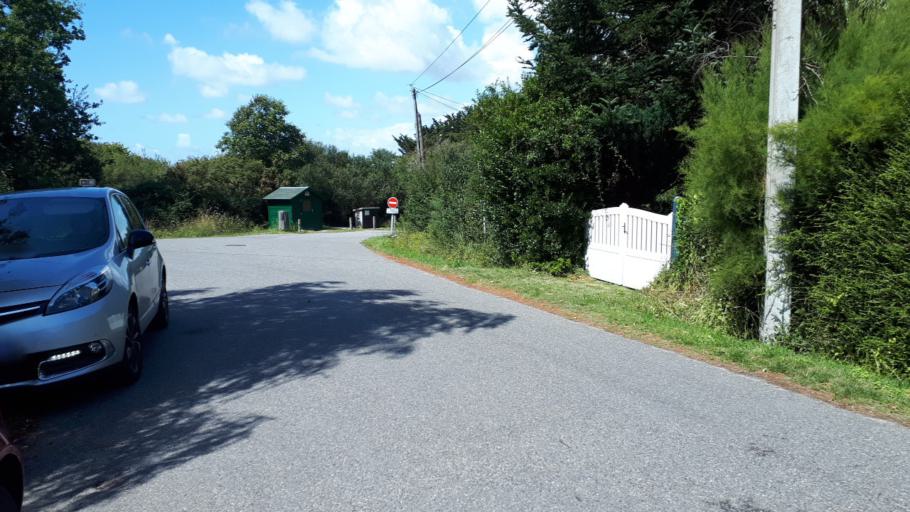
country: FR
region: Brittany
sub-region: Departement du Morbihan
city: Penestin
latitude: 47.4946
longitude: -2.4946
